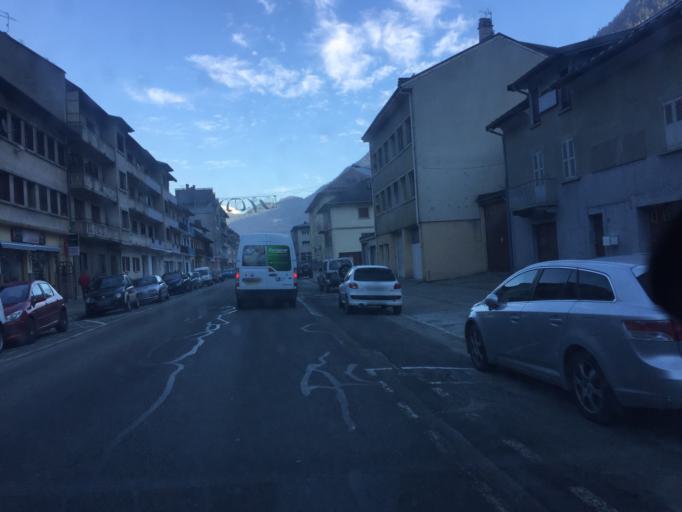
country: FR
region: Rhone-Alpes
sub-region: Departement de la Savoie
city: Modane
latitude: 45.1913
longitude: 6.6485
